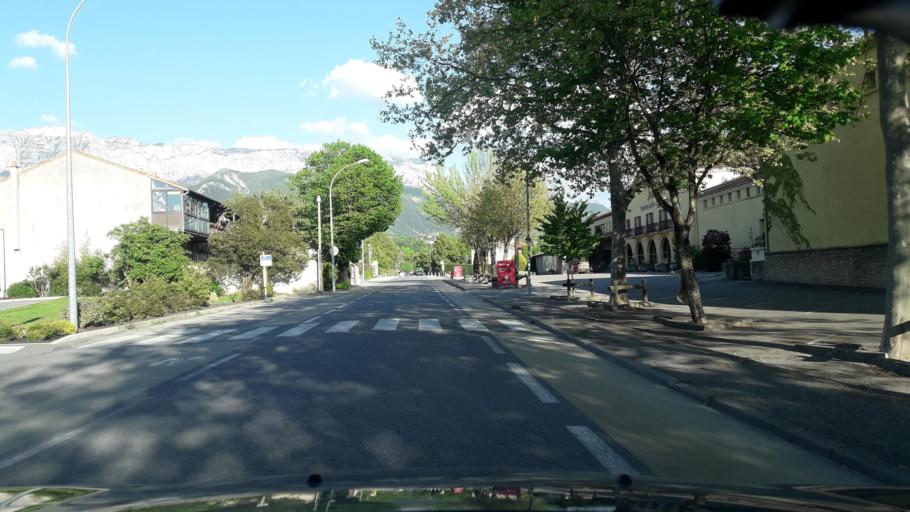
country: FR
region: Rhone-Alpes
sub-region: Departement de la Drome
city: Die
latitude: 44.7607
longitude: 5.3566
